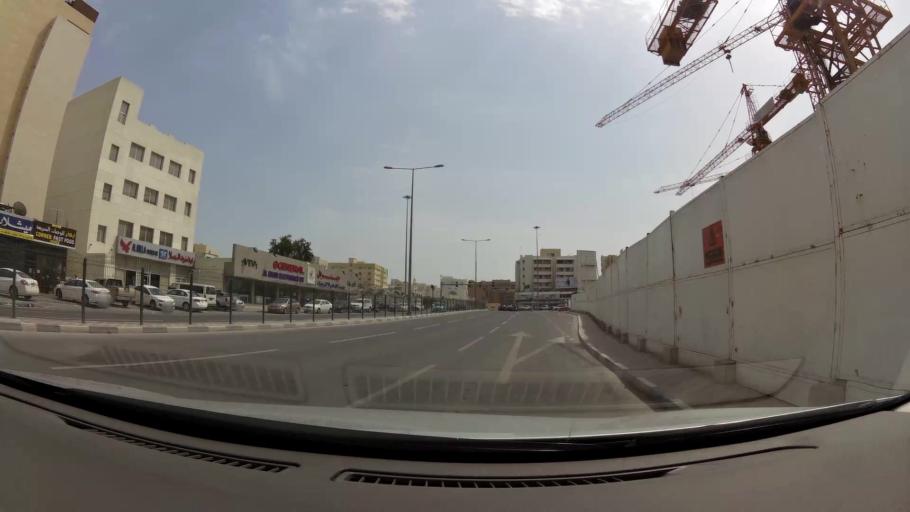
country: QA
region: Baladiyat ad Dawhah
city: Doha
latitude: 25.2839
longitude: 51.5441
